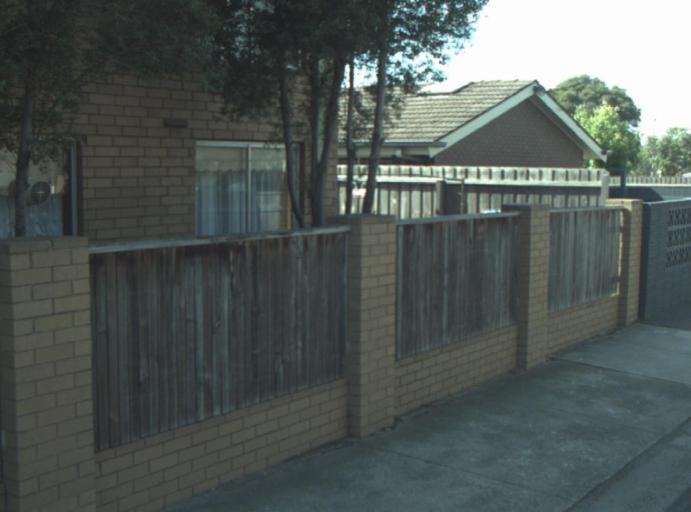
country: AU
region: Victoria
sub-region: Greater Geelong
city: Geelong West
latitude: -38.1400
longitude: 144.3400
